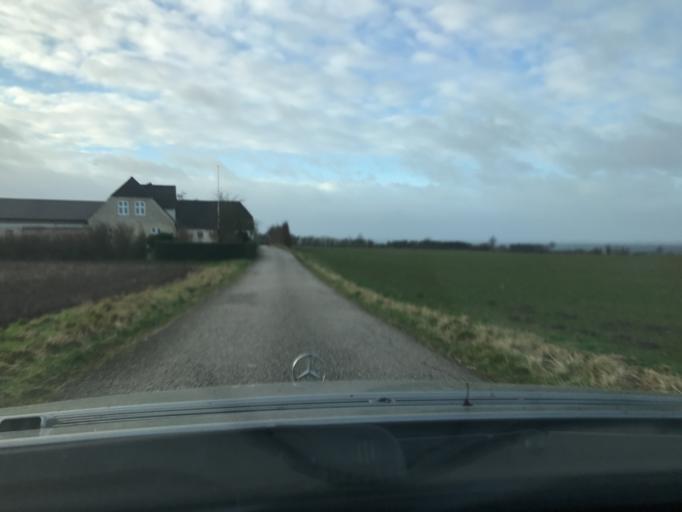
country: DK
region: South Denmark
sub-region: Sonderborg Kommune
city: Nordborg
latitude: 55.0510
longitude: 9.6704
